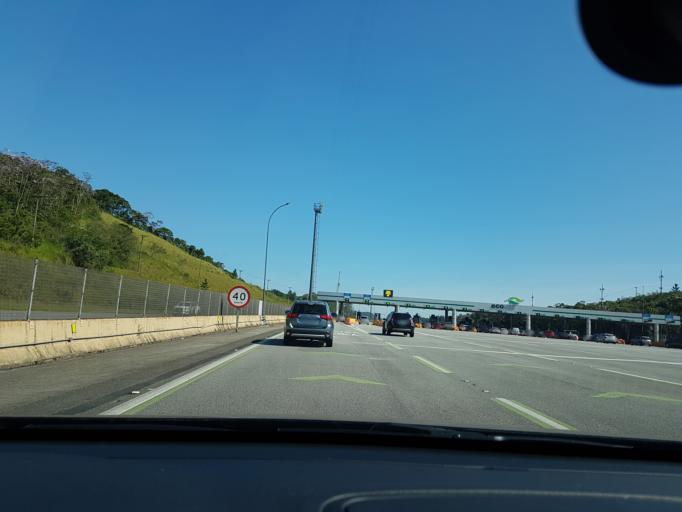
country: BR
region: Sao Paulo
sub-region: Sao Bernardo Do Campo
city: Sao Bernardo do Campo
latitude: -23.8193
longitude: -46.5827
